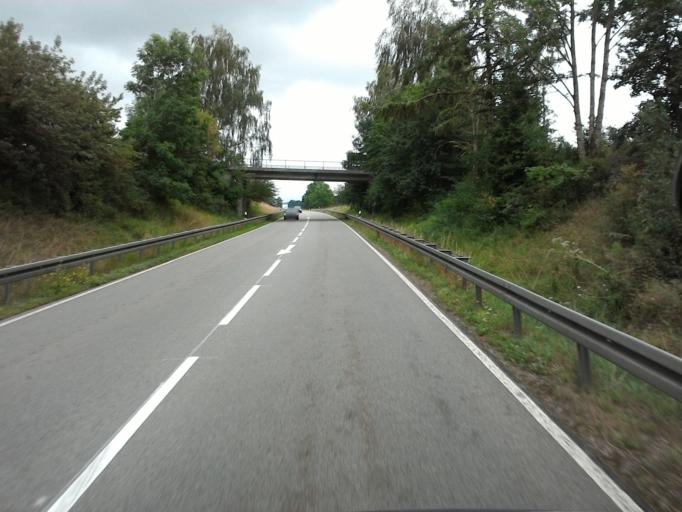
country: DE
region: Bavaria
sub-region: Upper Bavaria
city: Weyarn
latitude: 47.8281
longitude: 11.8248
